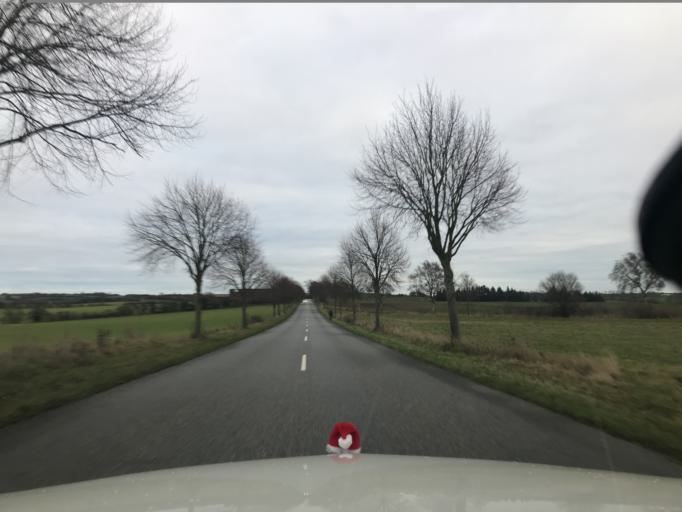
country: DK
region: South Denmark
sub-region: Sonderborg Kommune
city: Broager
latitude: 54.8872
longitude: 9.6883
